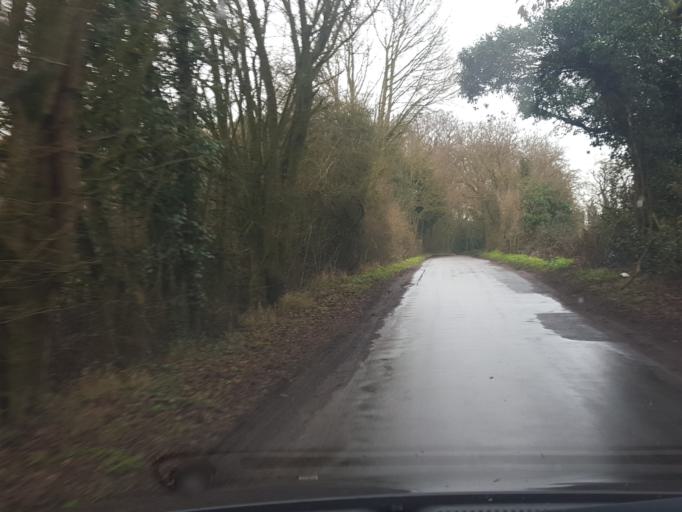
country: GB
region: England
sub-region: Essex
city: West Bergholt
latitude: 51.9316
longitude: 0.8456
